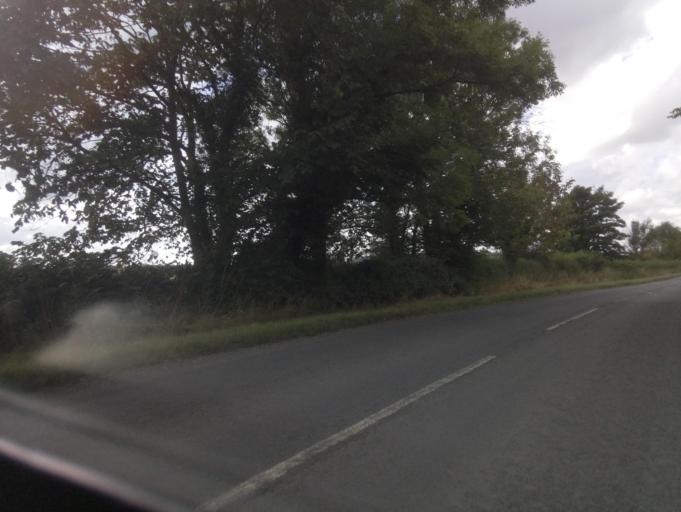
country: GB
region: England
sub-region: North Yorkshire
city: Bedale
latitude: 54.2338
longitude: -1.6712
